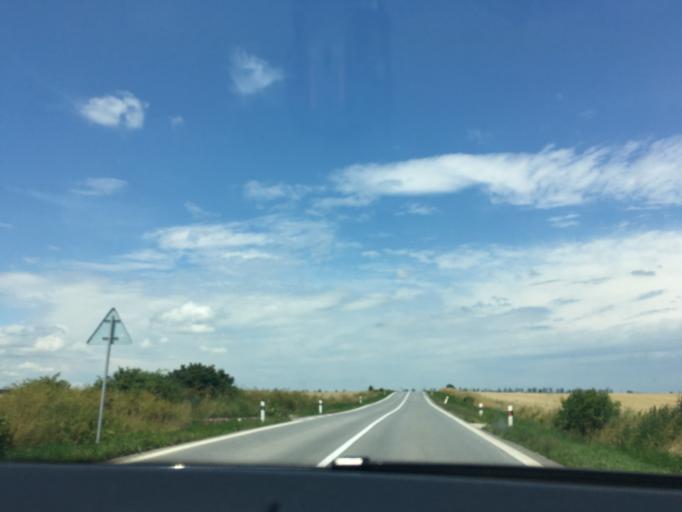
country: SK
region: Presovsky
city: Vranov nad Topl'ou
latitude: 48.7956
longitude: 21.6820
